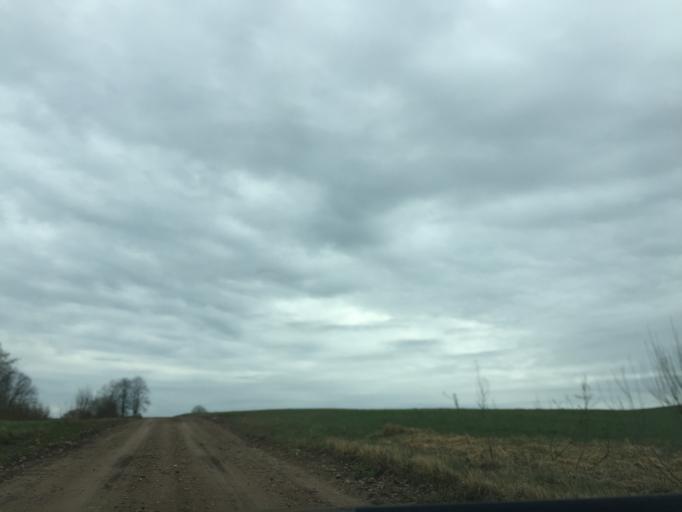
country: LV
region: Malpils
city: Malpils
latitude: 57.0272
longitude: 24.8443
